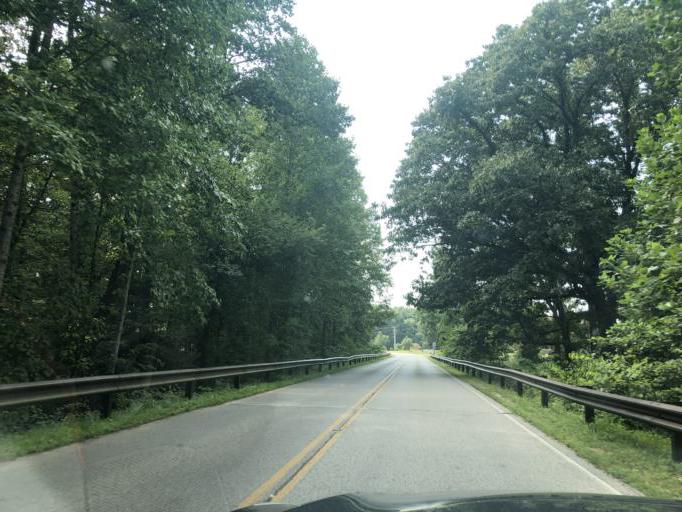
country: US
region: Tennessee
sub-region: Franklin County
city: Sewanee
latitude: 35.2083
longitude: -85.9116
